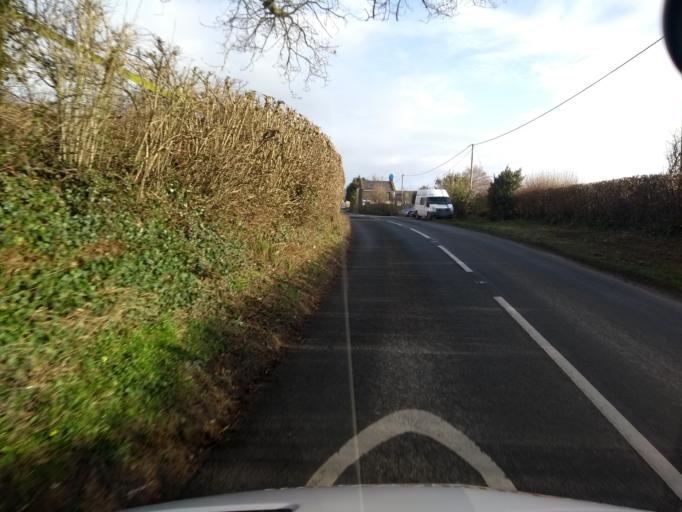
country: GB
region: England
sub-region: Somerset
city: Castle Cary
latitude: 51.0582
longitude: -2.5284
